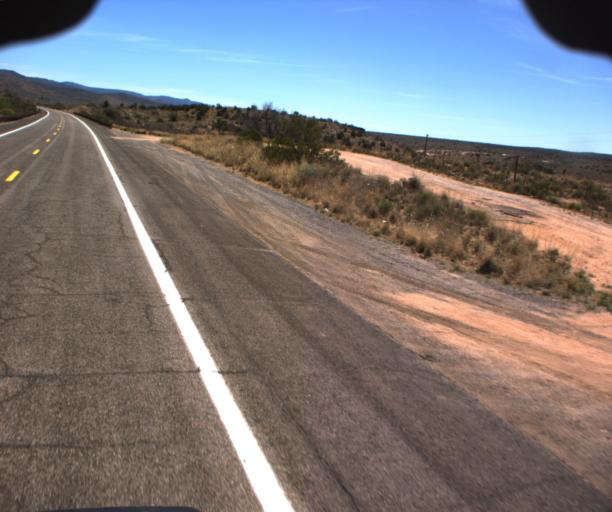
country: US
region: Arizona
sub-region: Mohave County
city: Peach Springs
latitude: 35.3685
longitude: -113.7143
